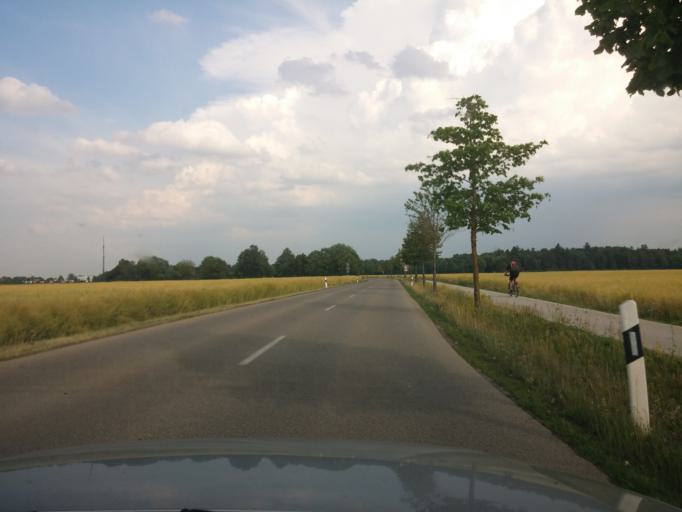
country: DE
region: Bavaria
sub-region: Upper Bavaria
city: Haar
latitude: 48.1255
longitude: 11.7454
